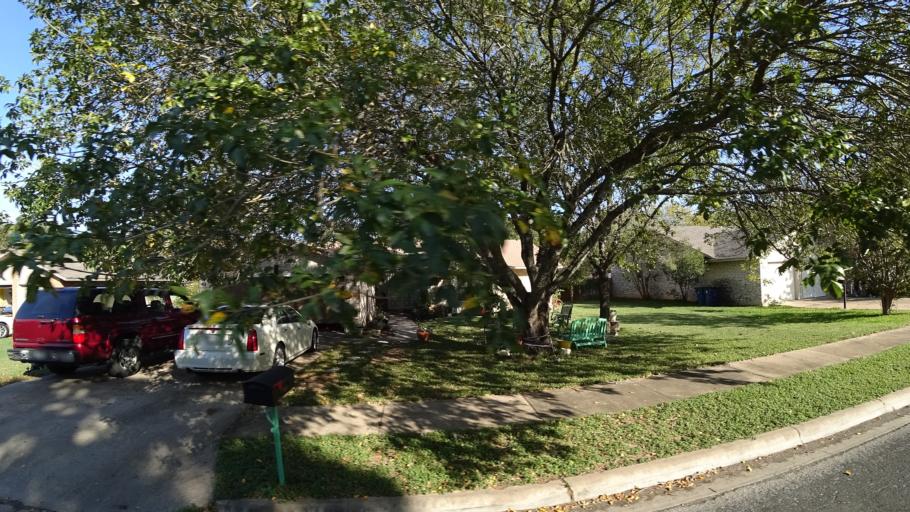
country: US
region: Texas
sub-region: Williamson County
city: Anderson Mill
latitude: 30.4481
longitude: -97.8085
